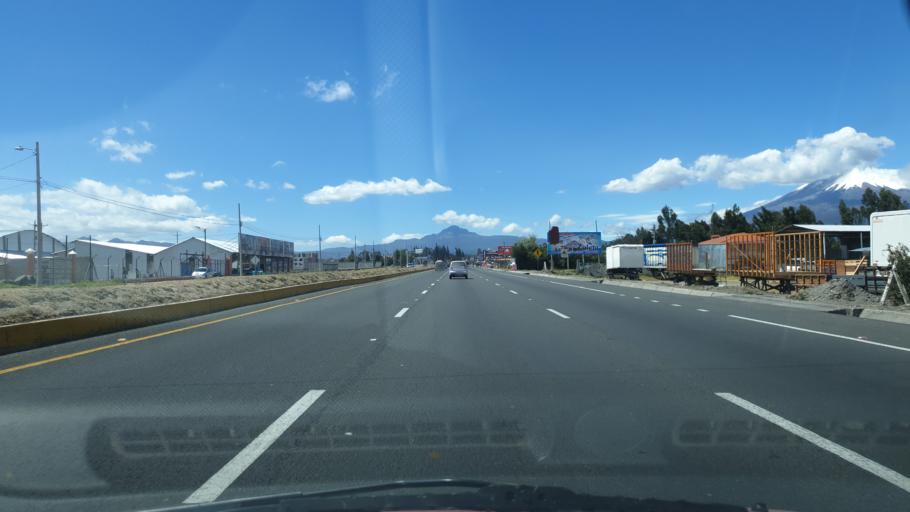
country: EC
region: Cotopaxi
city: Saquisili
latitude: -0.8083
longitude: -78.6231
